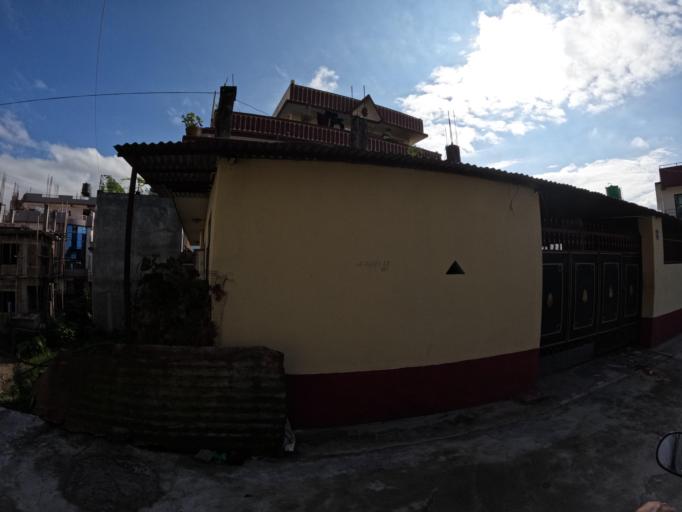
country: NP
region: Central Region
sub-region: Bagmati Zone
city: Kathmandu
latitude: 27.7607
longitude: 85.3317
